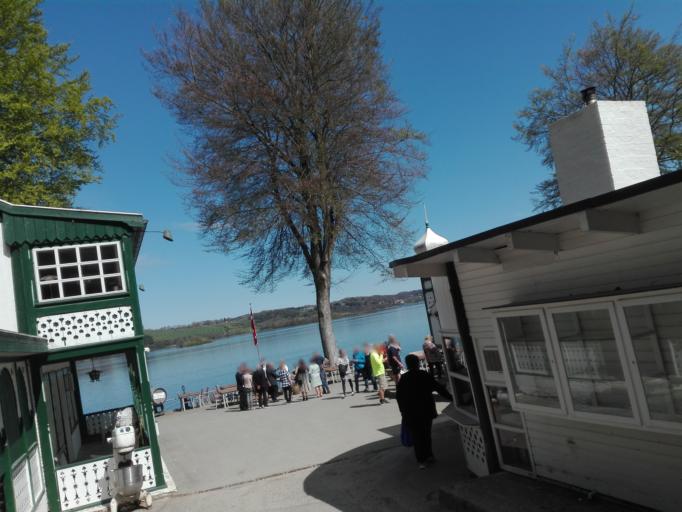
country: DK
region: Central Jutland
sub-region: Silkeborg Kommune
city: Svejbaek
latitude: 56.1098
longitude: 9.6844
